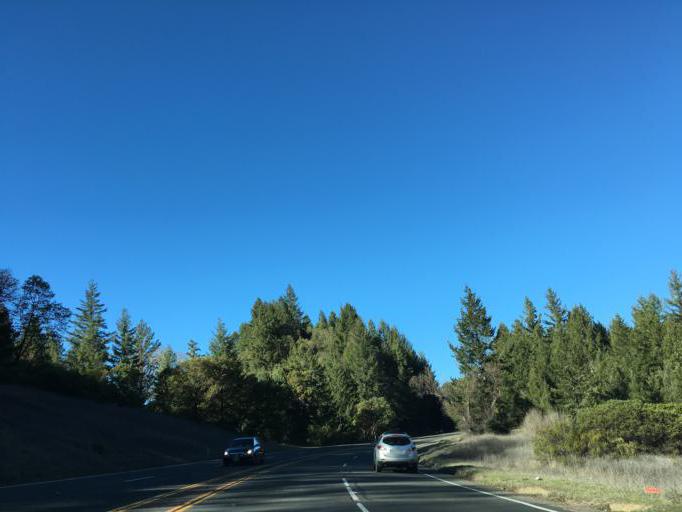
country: US
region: California
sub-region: Mendocino County
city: Brooktrails
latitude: 39.5371
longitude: -123.4171
